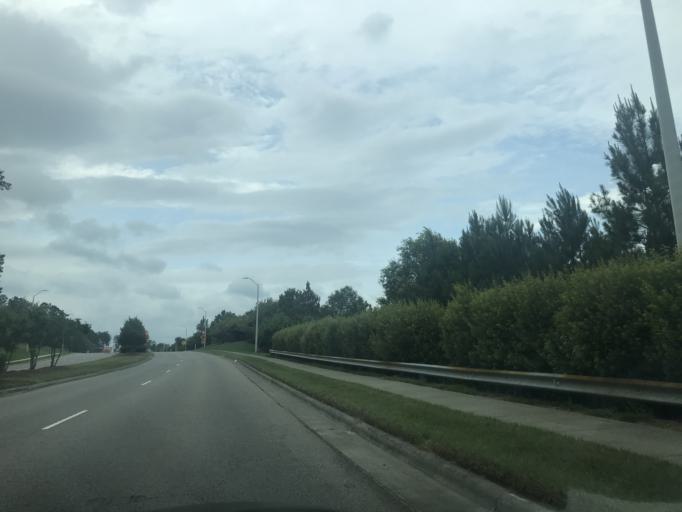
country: US
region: North Carolina
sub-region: Wake County
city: Green Level
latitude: 35.8062
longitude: -78.9022
